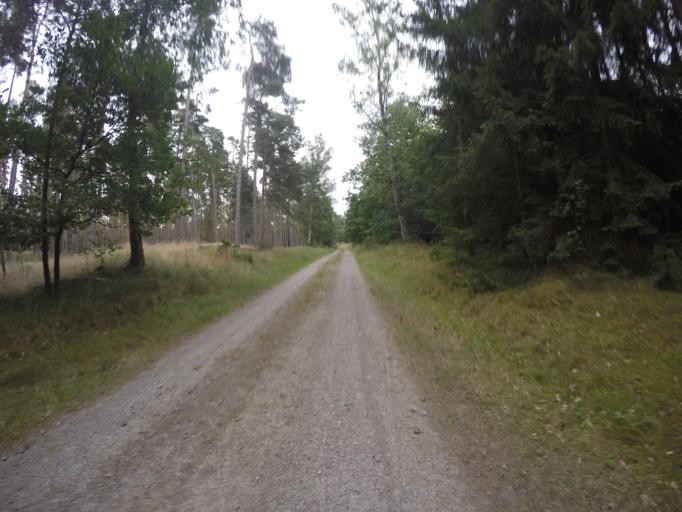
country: DE
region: Lower Saxony
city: Thomasburg
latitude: 53.2428
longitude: 10.7027
